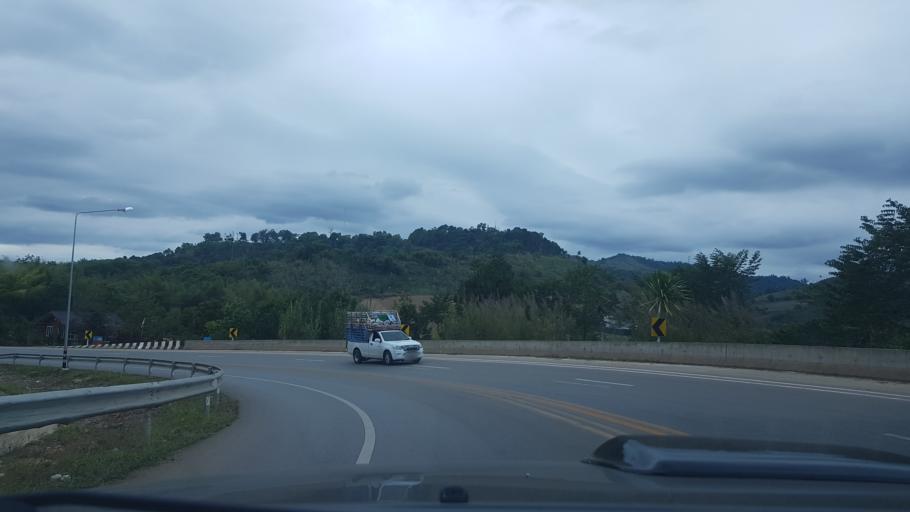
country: TH
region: Phetchabun
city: Khao Kho
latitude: 16.5703
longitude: 100.9980
